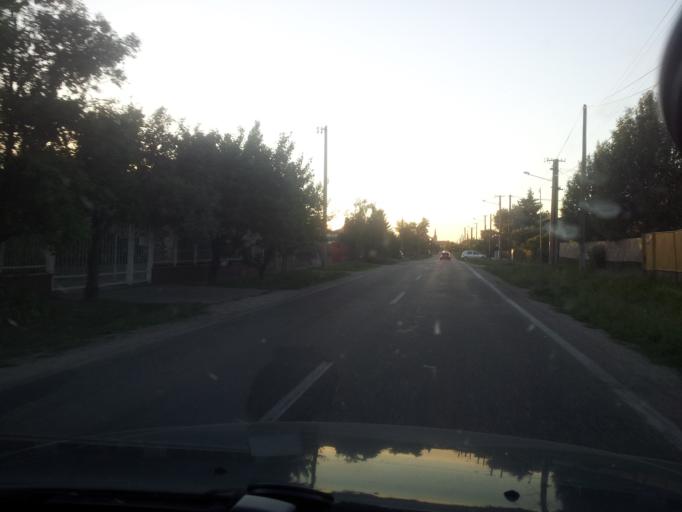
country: SK
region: Nitriansky
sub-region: Okres Nove Zamky
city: Sturovo
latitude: 47.8457
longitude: 18.6605
